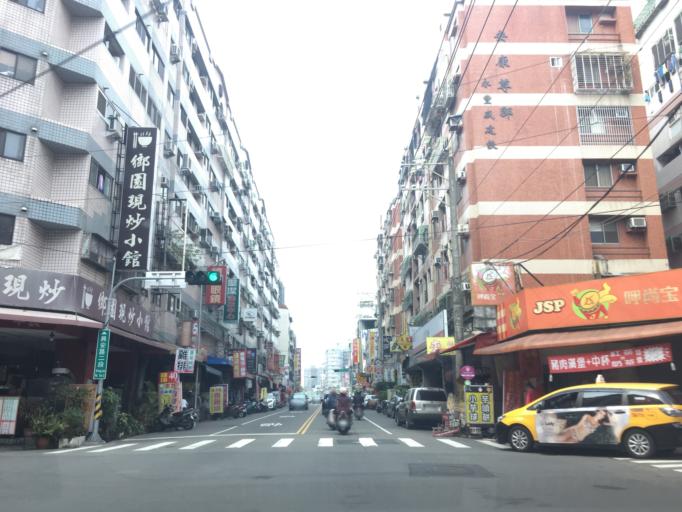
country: TW
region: Taiwan
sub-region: Taichung City
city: Taichung
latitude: 24.1753
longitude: 120.6947
